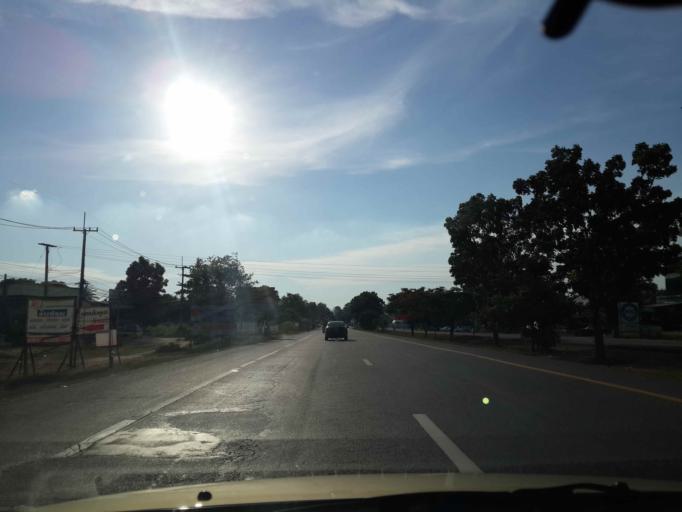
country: TH
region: Chon Buri
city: Bang Lamung
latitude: 12.9773
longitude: 100.9620
